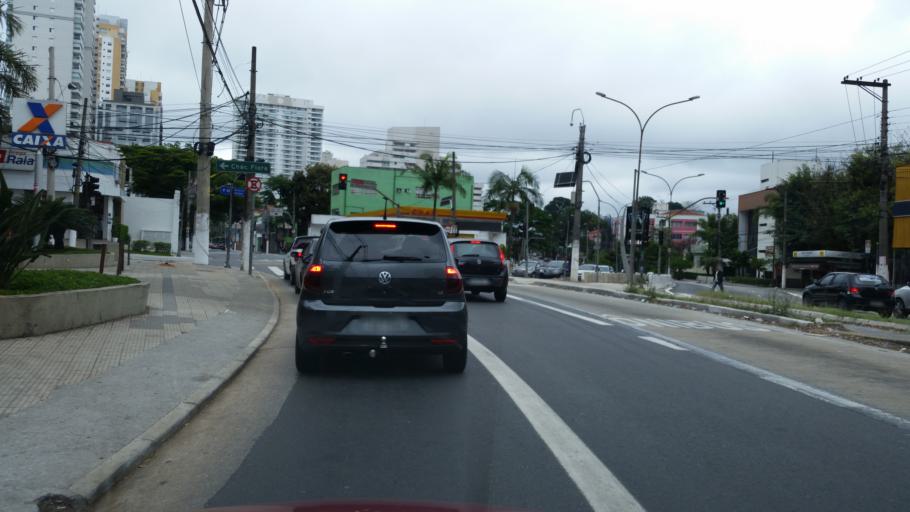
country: BR
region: Sao Paulo
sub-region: Diadema
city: Diadema
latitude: -23.6436
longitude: -46.7009
